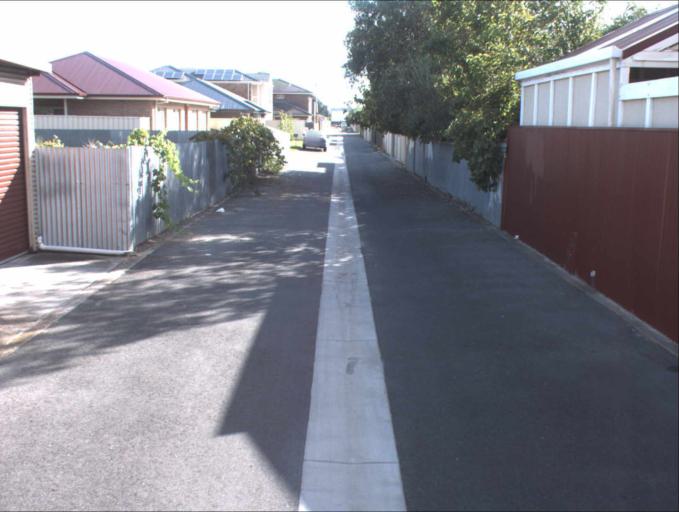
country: AU
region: South Australia
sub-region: Port Adelaide Enfield
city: Klemzig
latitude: -34.8770
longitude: 138.6286
